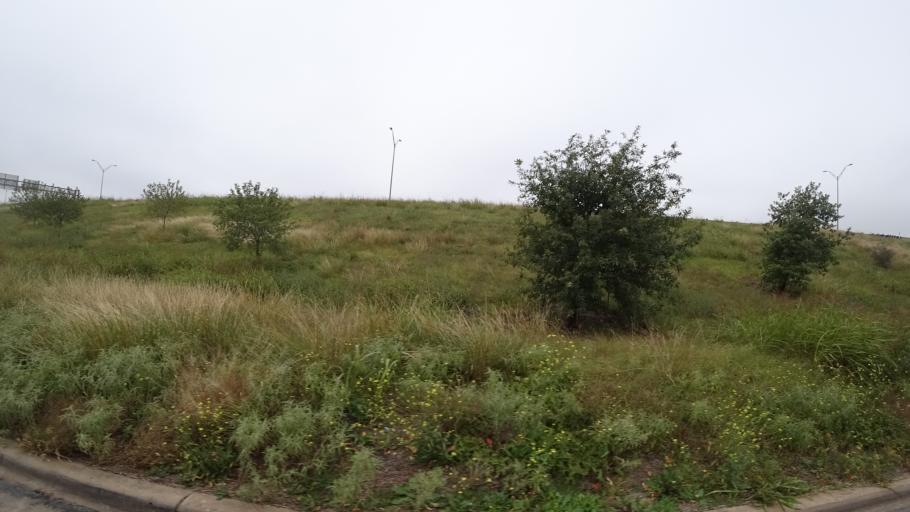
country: US
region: Texas
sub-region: Travis County
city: Shady Hollow
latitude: 30.2190
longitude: -97.8367
